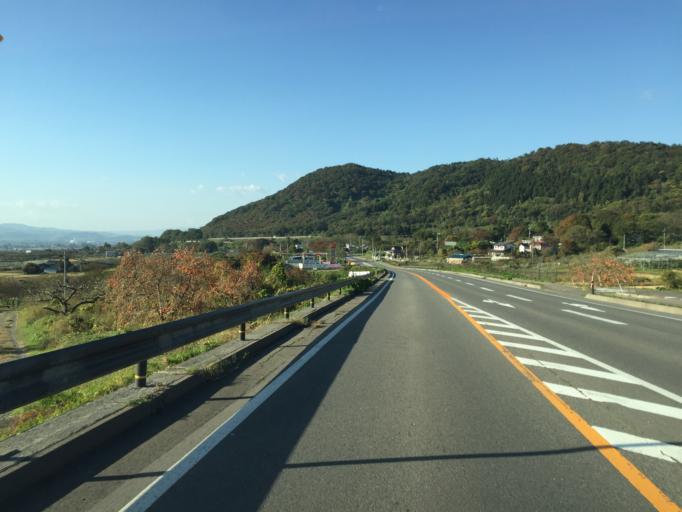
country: JP
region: Fukushima
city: Yanagawamachi-saiwaicho
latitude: 37.9017
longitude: 140.5757
